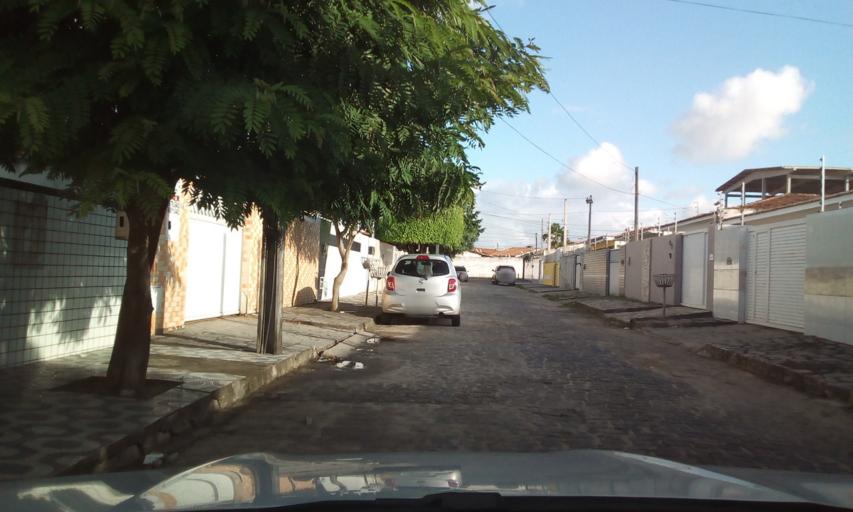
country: BR
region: Paraiba
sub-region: Joao Pessoa
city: Joao Pessoa
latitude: -7.1725
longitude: -34.8654
